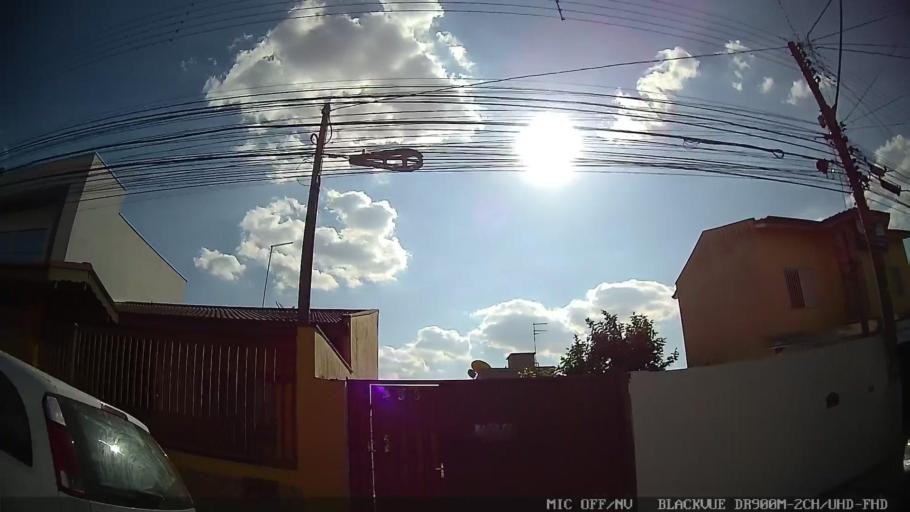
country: BR
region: Sao Paulo
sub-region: Cabreuva
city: Cabreuva
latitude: -23.2516
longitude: -47.0544
